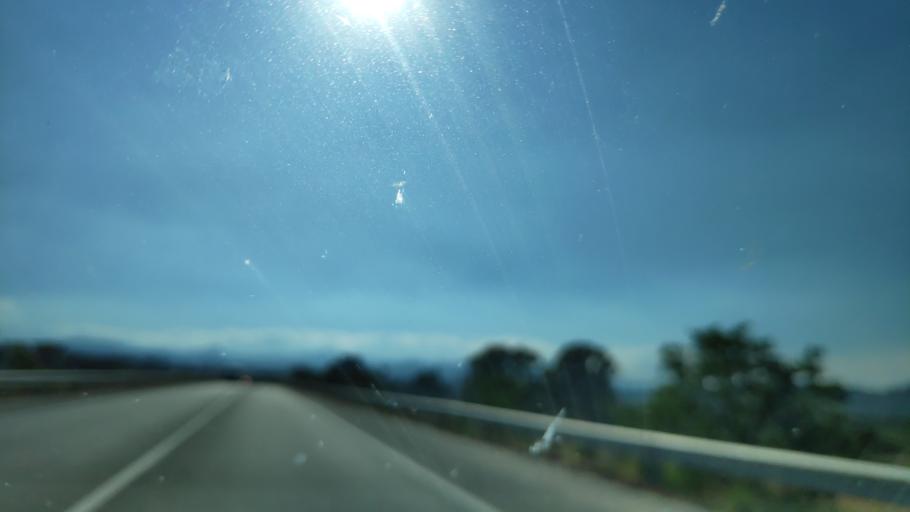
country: IT
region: Calabria
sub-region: Provincia di Reggio Calabria
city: Marina di Gioiosa Ionica
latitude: 38.3067
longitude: 16.3438
